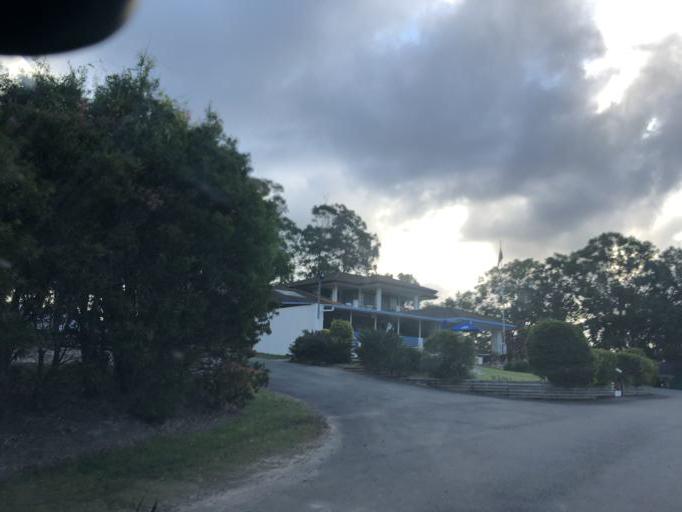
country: AU
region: New South Wales
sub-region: Coffs Harbour
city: Woolgoolga
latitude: -30.0944
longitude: 153.1941
